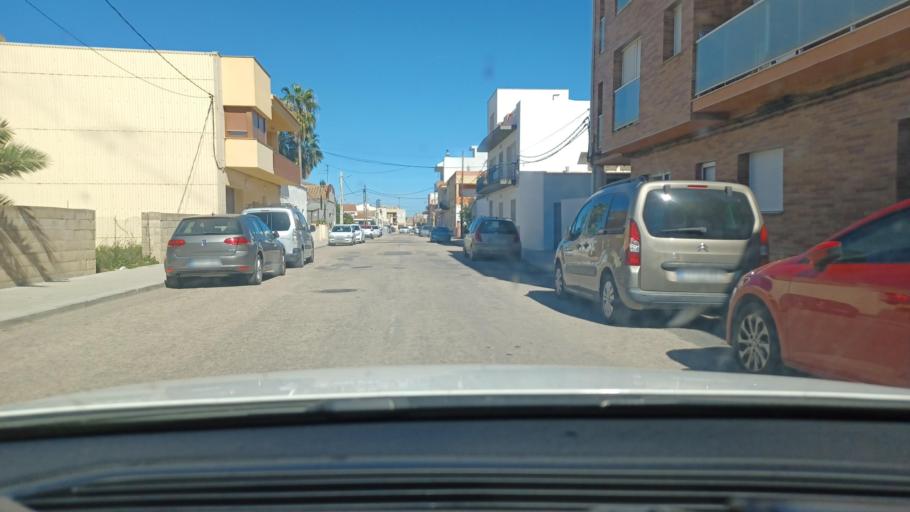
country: ES
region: Catalonia
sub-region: Provincia de Tarragona
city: Deltebre
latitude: 40.7174
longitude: 0.7401
